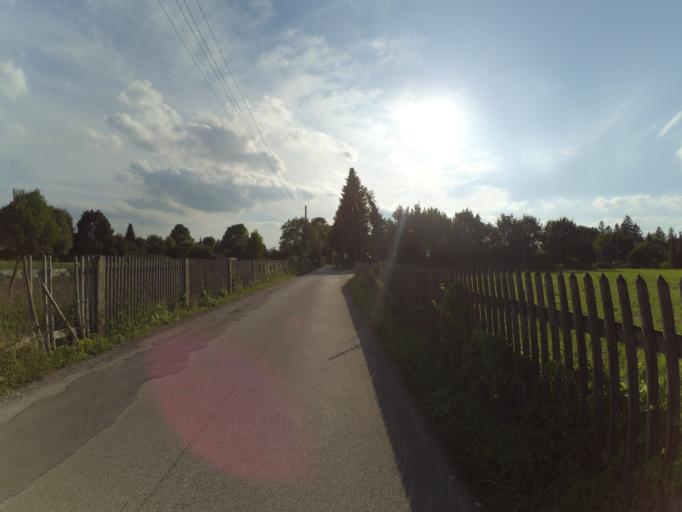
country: DE
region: Bavaria
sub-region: Upper Bavaria
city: Karlsfeld
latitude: 48.1878
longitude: 11.4981
